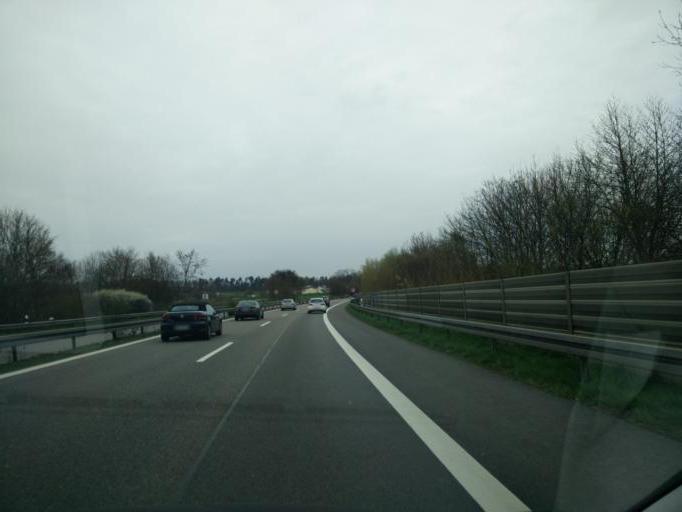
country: DE
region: Baden-Wuerttemberg
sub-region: Tuebingen Region
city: Pliezhausen
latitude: 48.5896
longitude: 9.1694
